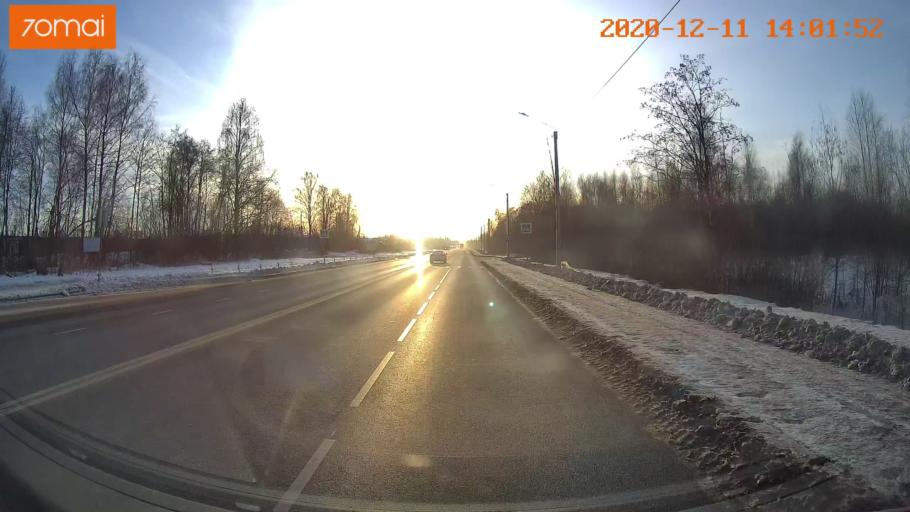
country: RU
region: Kostroma
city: Oktyabr'skiy
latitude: 57.7793
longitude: 41.0326
